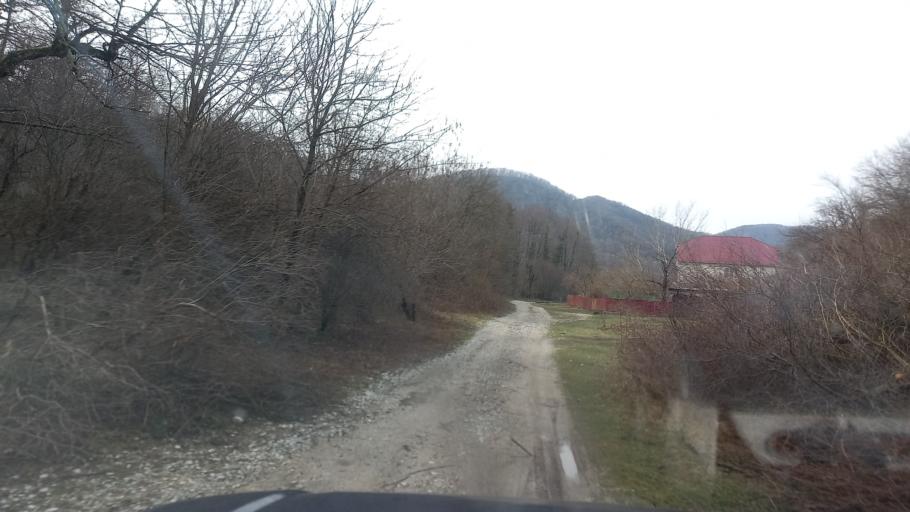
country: RU
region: Krasnodarskiy
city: Dzhubga
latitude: 44.4160
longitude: 38.7213
